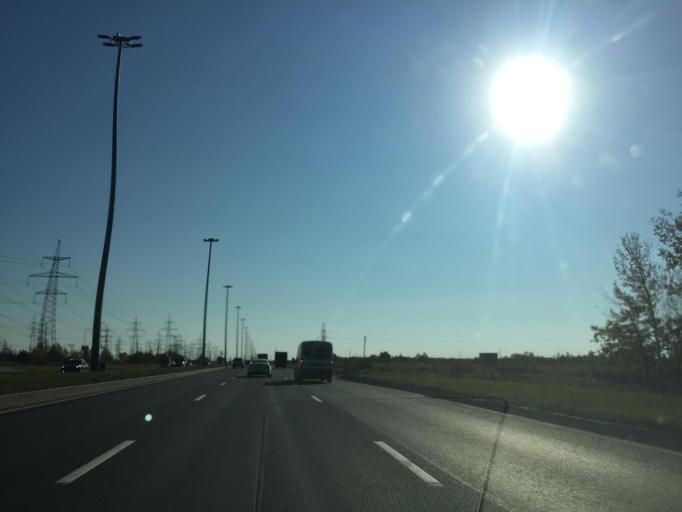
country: RU
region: St.-Petersburg
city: Petro-Slavyanka
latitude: 59.7612
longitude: 30.5105
